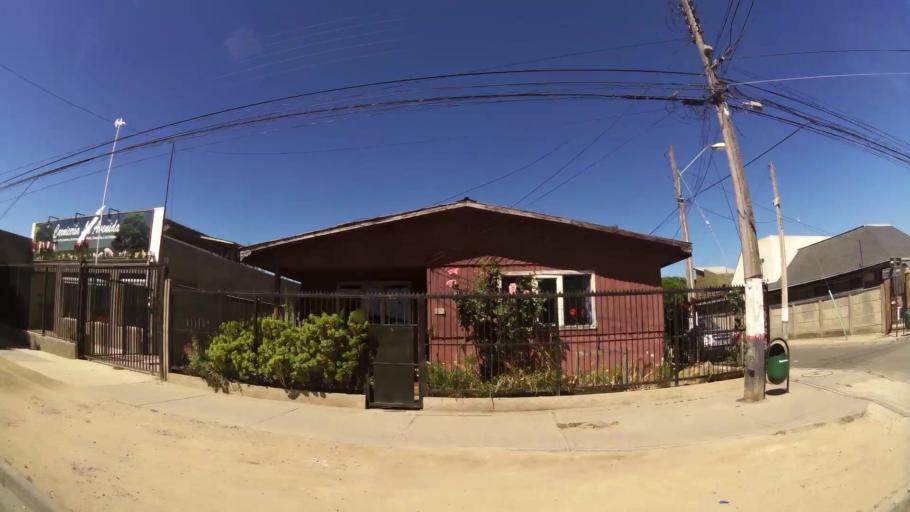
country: CL
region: Valparaiso
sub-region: Provincia de Marga Marga
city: Quilpue
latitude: -33.3167
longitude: -71.4019
